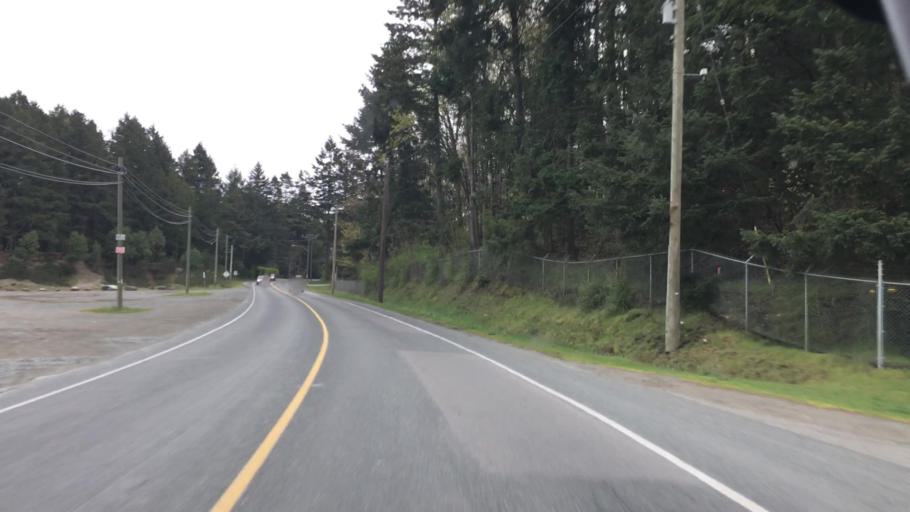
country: CA
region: British Columbia
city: North Saanich
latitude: 48.5652
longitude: -123.4284
